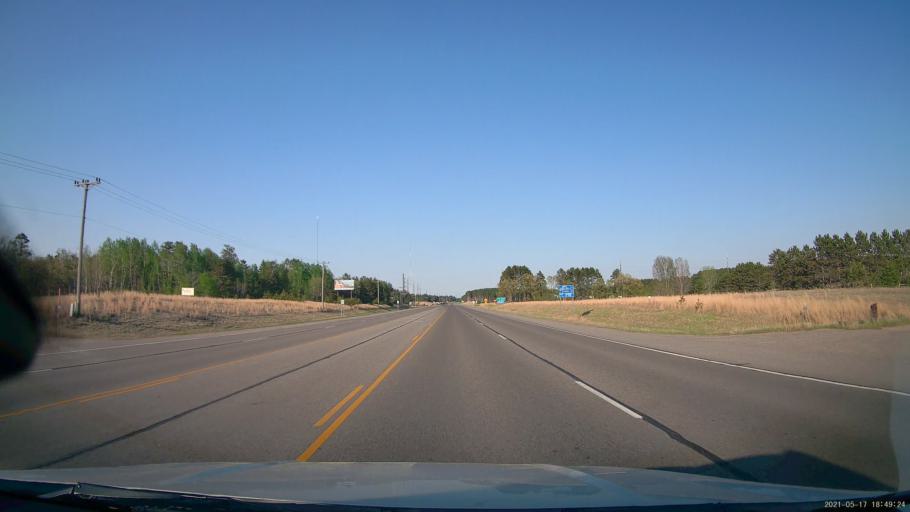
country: US
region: Minnesota
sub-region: Hubbard County
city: Park Rapids
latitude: 46.9242
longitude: -95.0205
